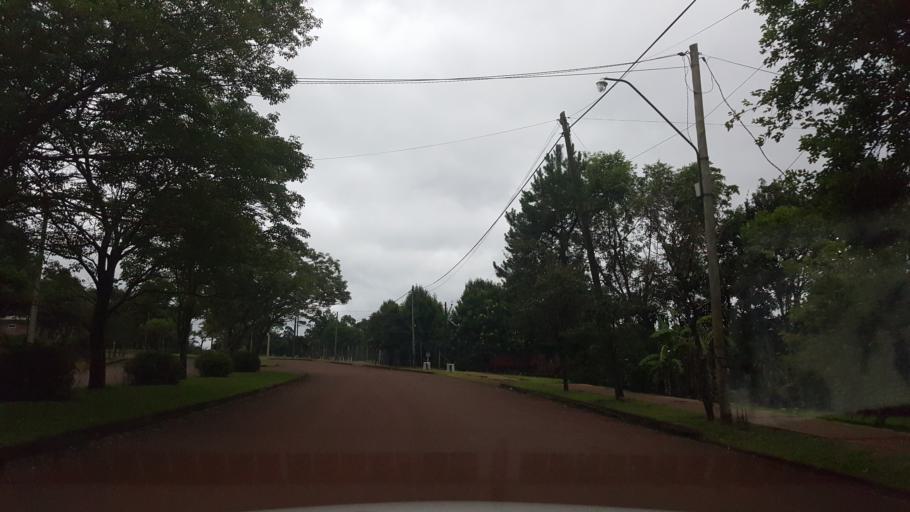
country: AR
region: Misiones
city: Ruiz de Montoya
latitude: -26.9808
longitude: -55.0498
